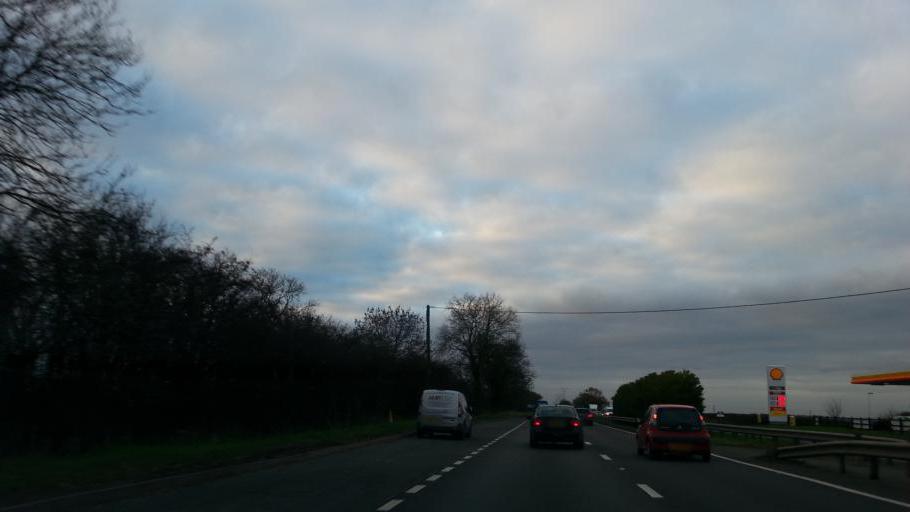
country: GB
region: England
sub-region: Leicestershire
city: Queniborough
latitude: 52.7544
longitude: -1.0593
